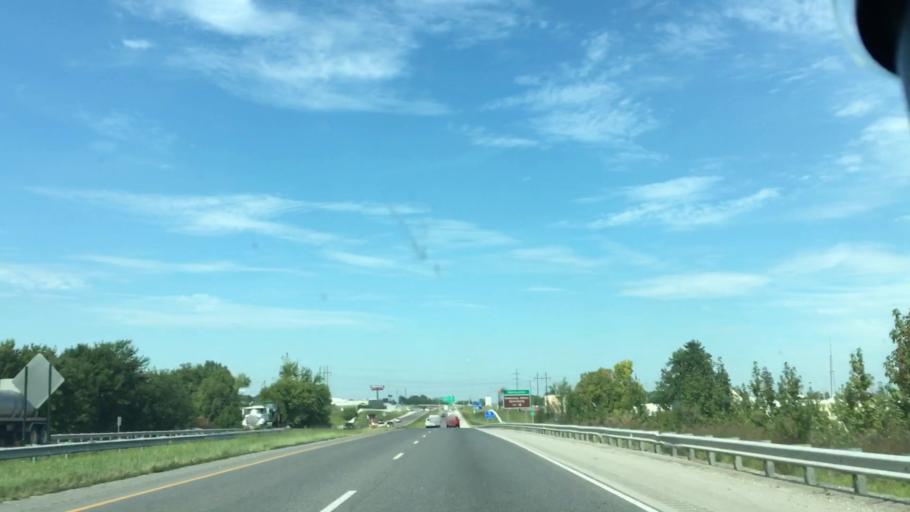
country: US
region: Kentucky
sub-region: Daviess County
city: Owensboro
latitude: 37.7470
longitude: -87.0713
